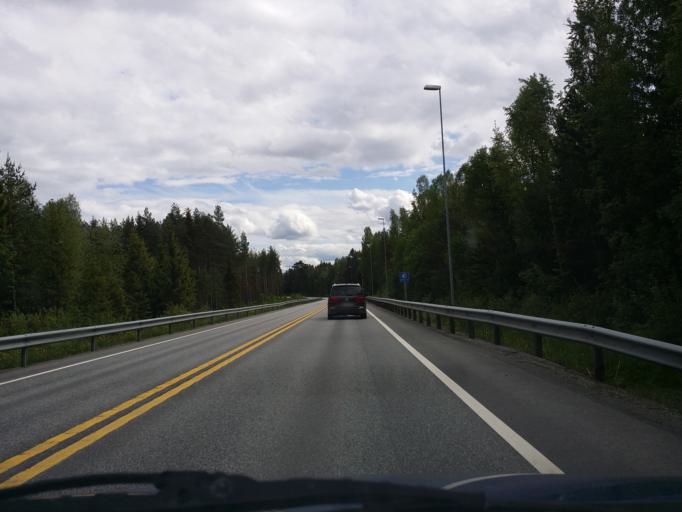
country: NO
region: Hedmark
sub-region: Stange
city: Stange
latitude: 60.7127
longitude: 11.2499
